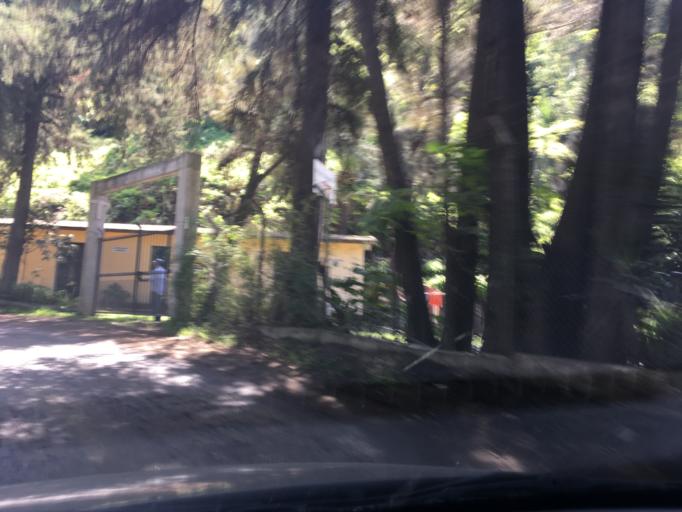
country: MX
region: Michoacan
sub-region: Morelia
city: La Mintzita (Piedra Dura)
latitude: 19.6398
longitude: -101.2736
